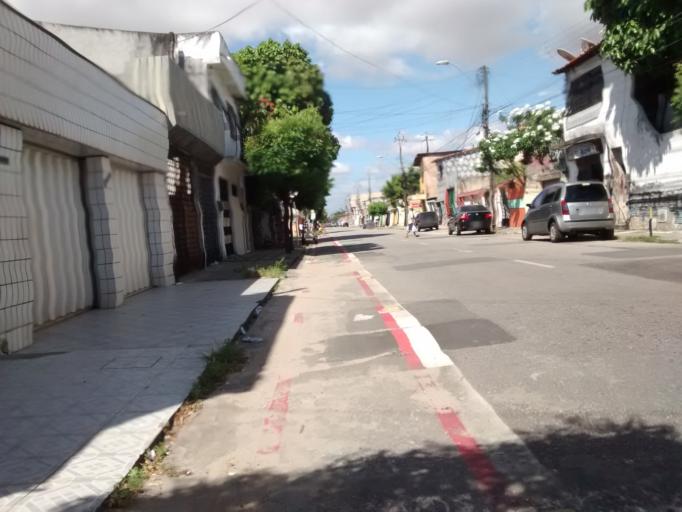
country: BR
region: Ceara
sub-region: Fortaleza
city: Fortaleza
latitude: -3.7275
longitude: -38.5516
